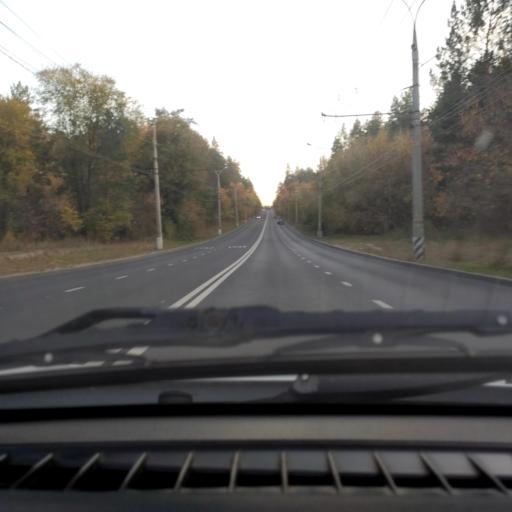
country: RU
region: Samara
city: Zhigulevsk
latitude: 53.5005
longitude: 49.4634
